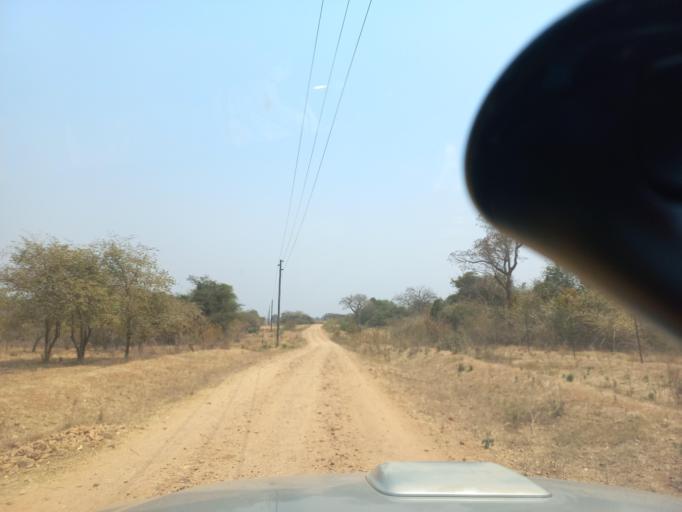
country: ZW
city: Chirundu
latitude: -15.9320
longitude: 28.8679
